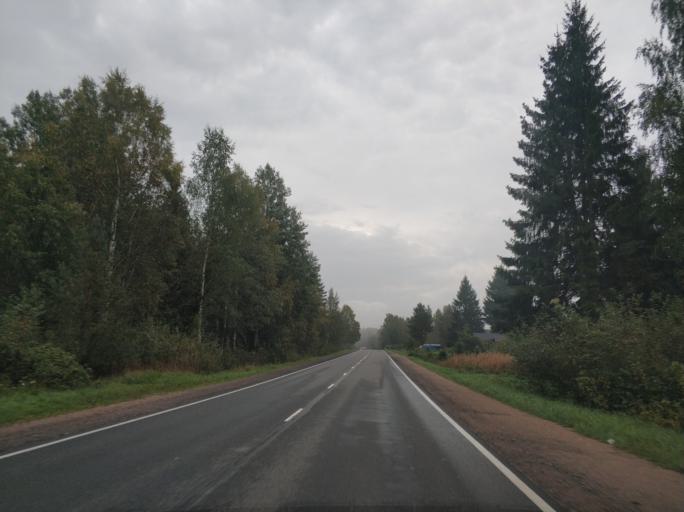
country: RU
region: Leningrad
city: Shcheglovo
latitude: 60.0956
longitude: 30.8469
